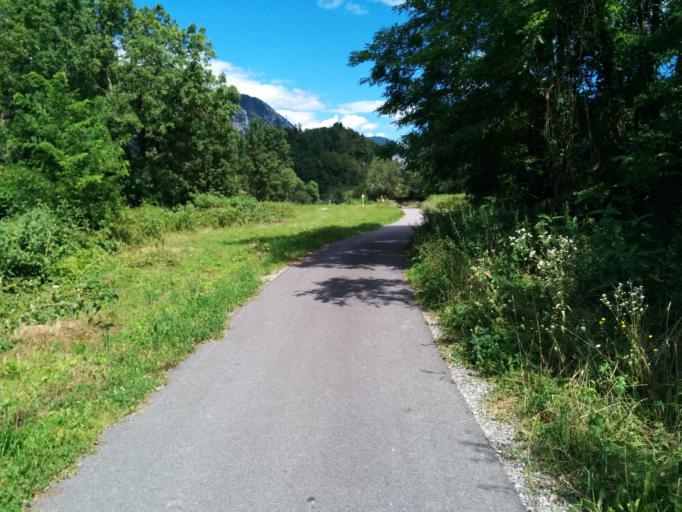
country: IT
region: Friuli Venezia Giulia
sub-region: Provincia di Udine
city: Villa Santina
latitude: 46.4045
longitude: 12.9329
